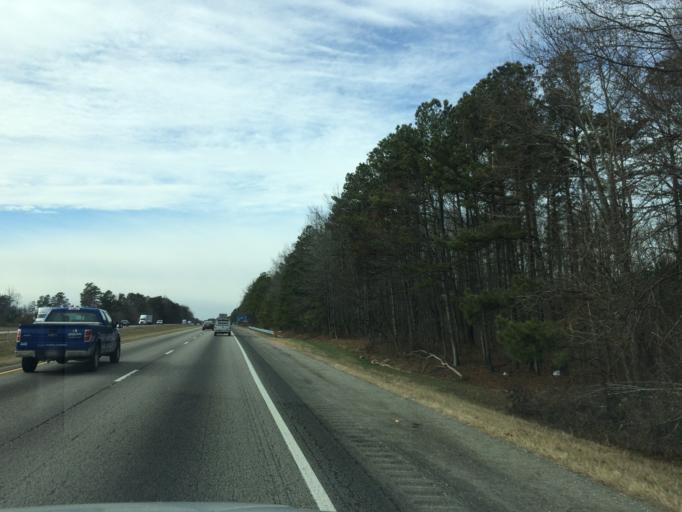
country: US
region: Georgia
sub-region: Gwinnett County
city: Dacula
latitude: 34.0767
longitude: -83.8990
